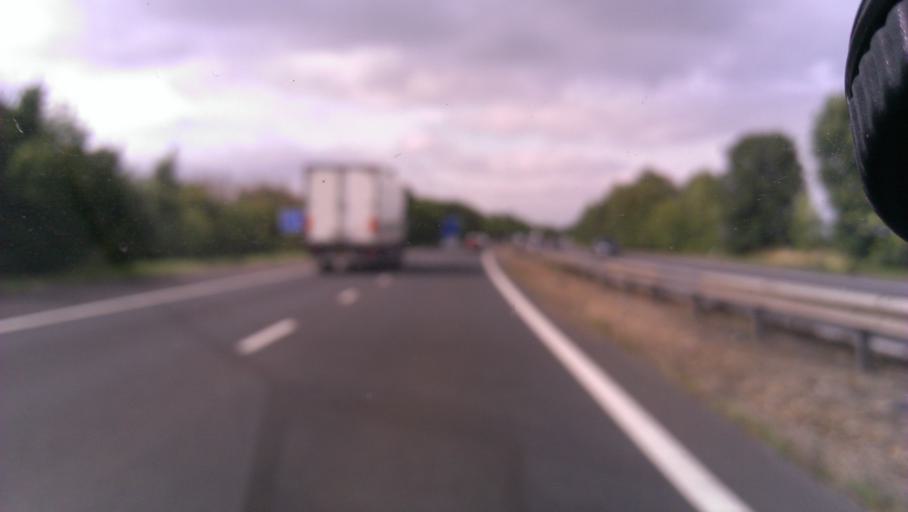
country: GB
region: England
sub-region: Cambridgeshire
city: Harston
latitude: 52.1360
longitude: 0.1126
